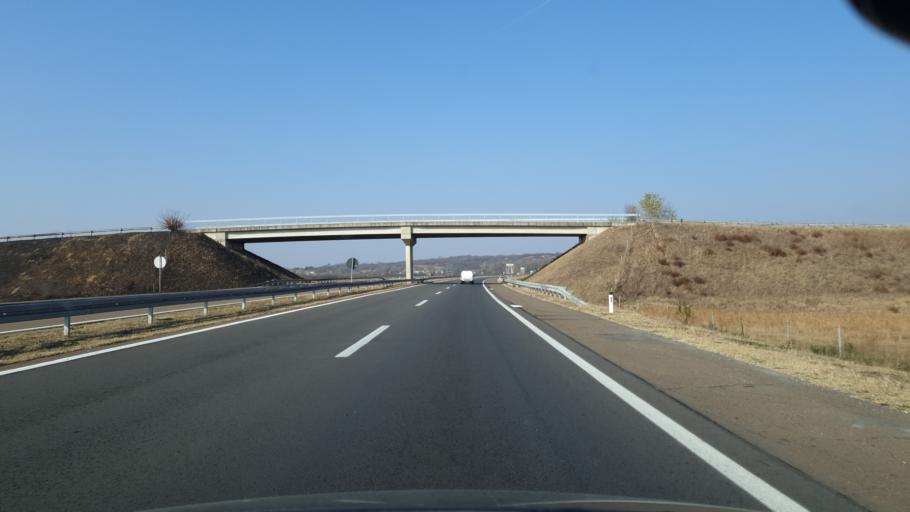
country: RS
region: Central Serbia
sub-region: Nisavski Okrug
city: Doljevac
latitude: 43.2037
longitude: 21.8410
